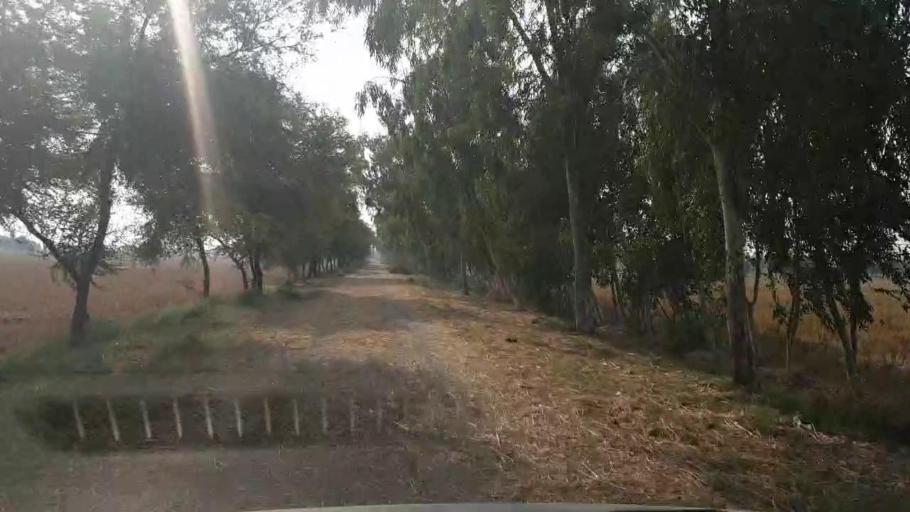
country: PK
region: Sindh
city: Tando Muhammad Khan
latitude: 25.0978
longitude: 68.5030
